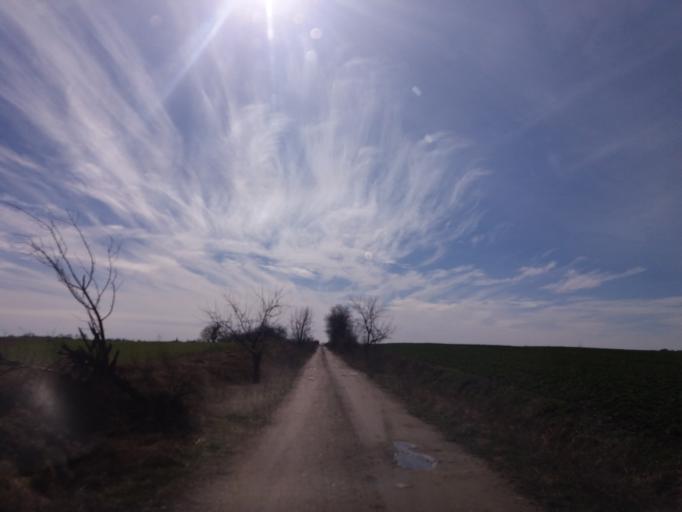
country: PL
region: West Pomeranian Voivodeship
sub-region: Powiat choszczenski
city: Choszczno
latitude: 53.1557
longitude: 15.3756
